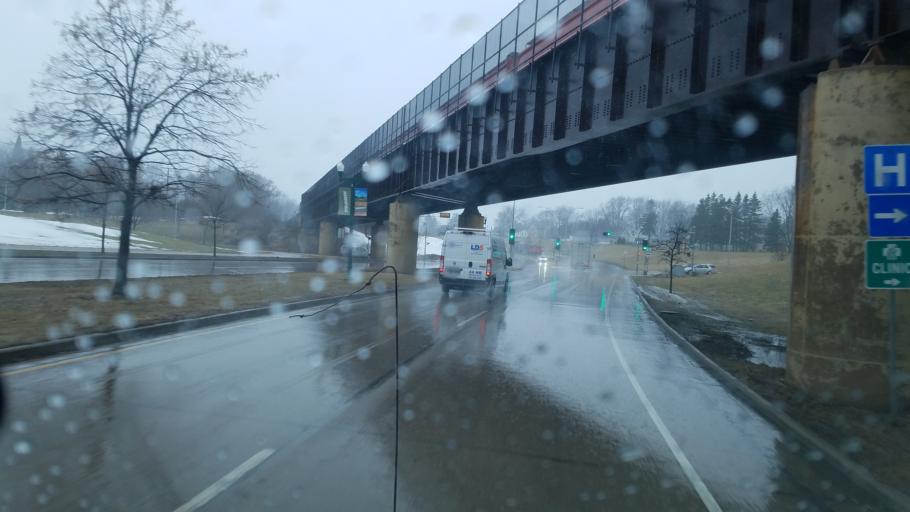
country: US
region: Wisconsin
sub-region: Wood County
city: Marshfield
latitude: 44.6699
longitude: -90.1811
